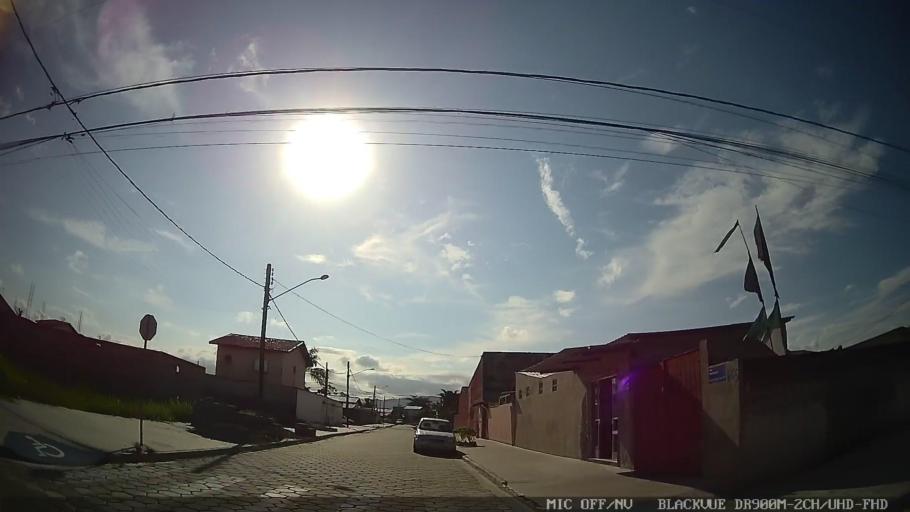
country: BR
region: Sao Paulo
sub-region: Itanhaem
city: Itanhaem
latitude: -24.1772
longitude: -46.8151
